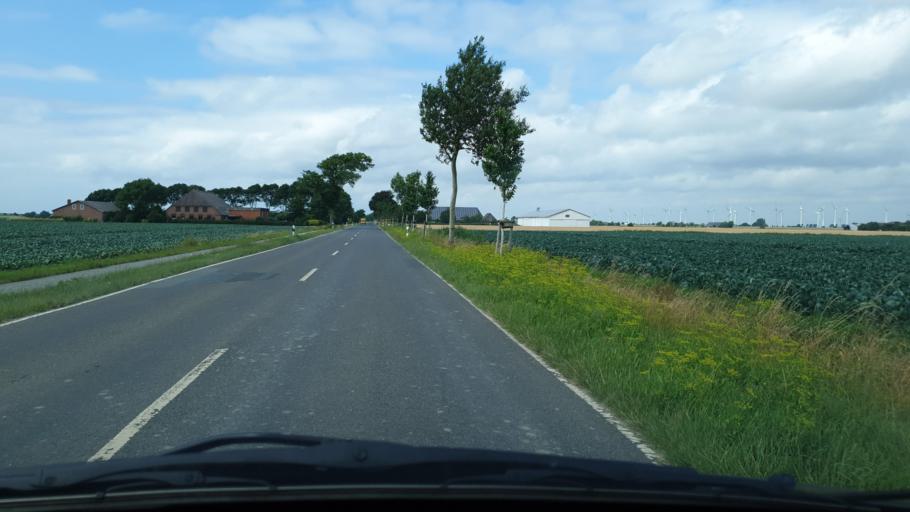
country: DE
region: Schleswig-Holstein
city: Friedrichskoog
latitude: 53.9778
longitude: 8.9198
